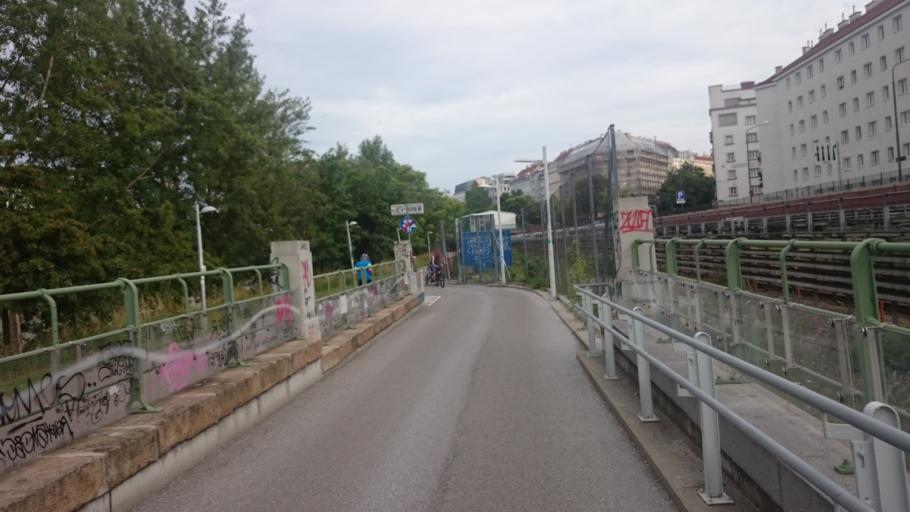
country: AT
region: Vienna
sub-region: Wien Stadt
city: Vienna
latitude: 48.2299
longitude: 16.3613
